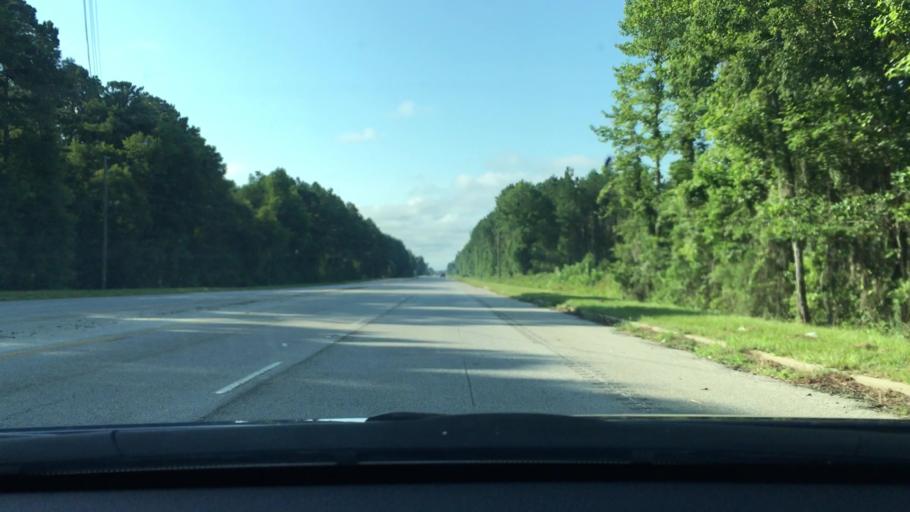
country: US
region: South Carolina
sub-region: Clarendon County
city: Manning
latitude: 33.7743
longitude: -80.2394
